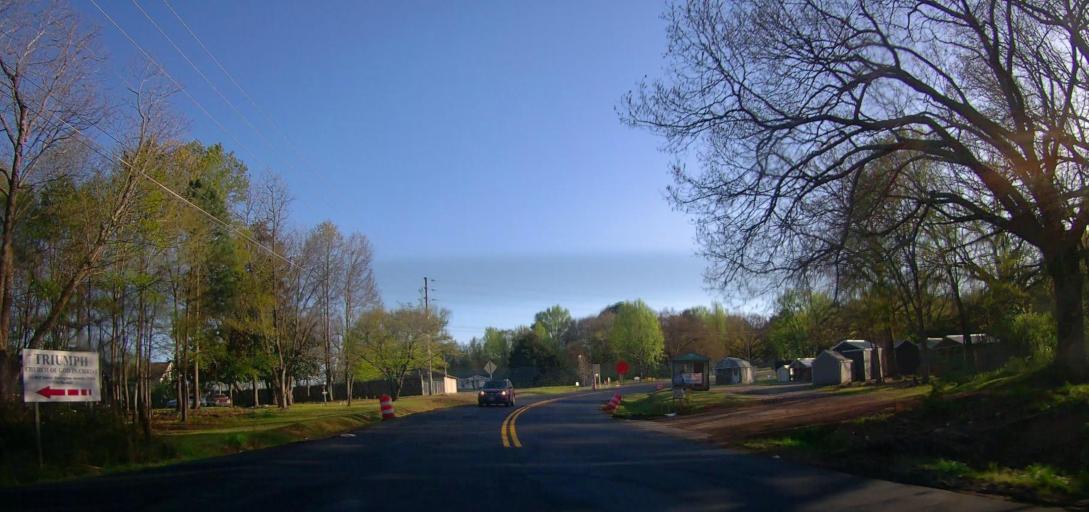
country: US
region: Georgia
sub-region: Newton County
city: Porterdale
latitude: 33.5548
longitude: -83.9064
